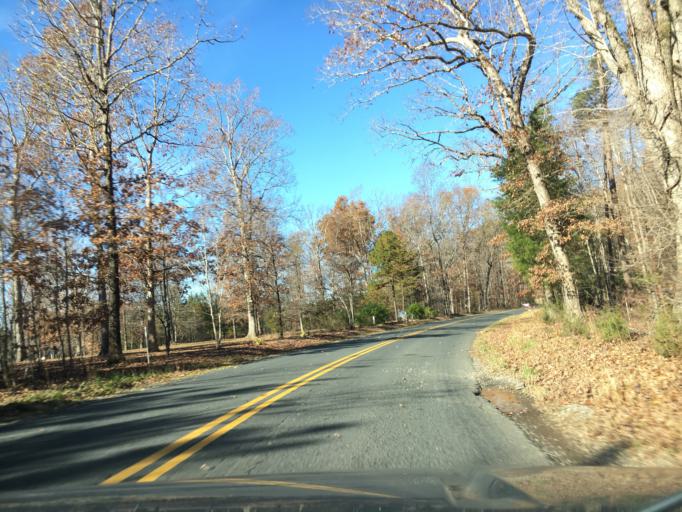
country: US
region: Virginia
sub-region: Buckingham County
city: Buckingham
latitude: 37.4207
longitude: -78.6094
